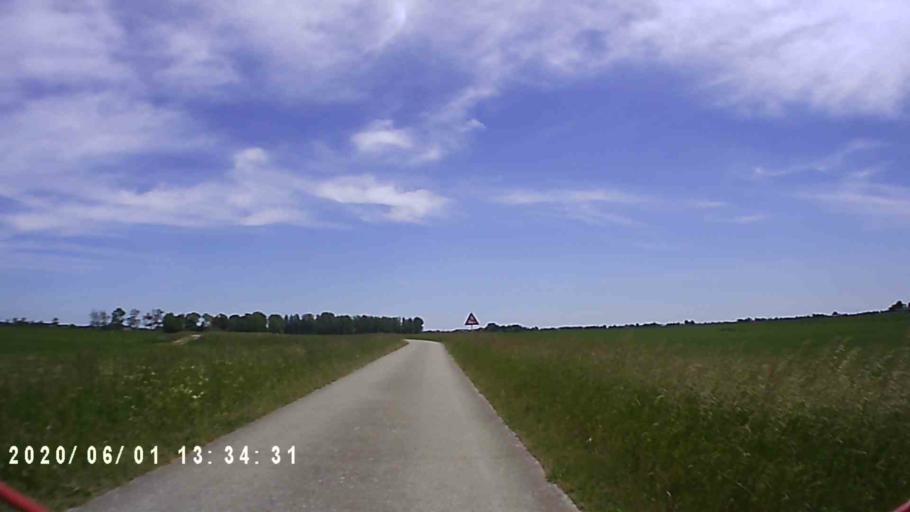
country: NL
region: Friesland
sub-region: Gemeente Littenseradiel
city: Wommels
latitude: 53.0903
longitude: 5.5738
